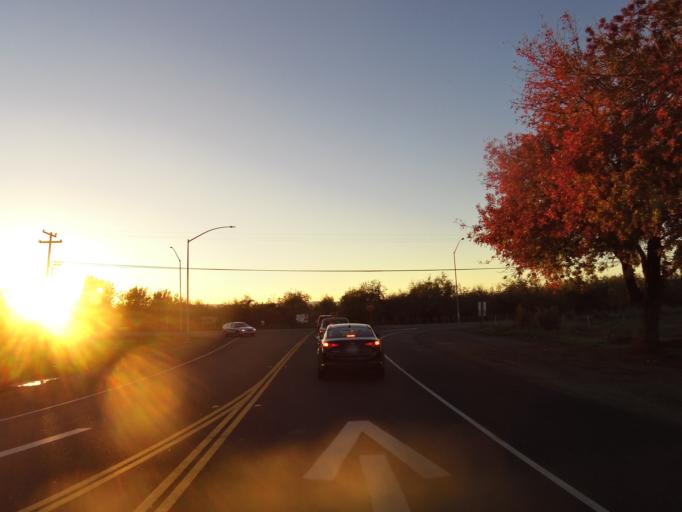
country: US
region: California
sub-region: Solano County
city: Dixon
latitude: 38.4613
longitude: -121.8402
